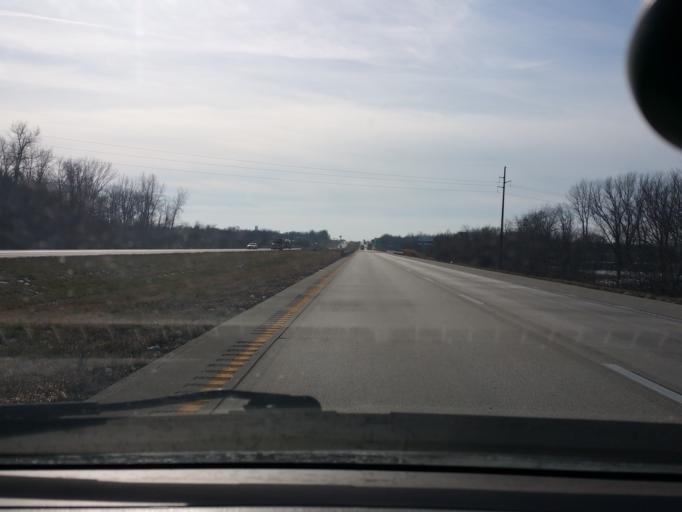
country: US
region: Missouri
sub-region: Clay County
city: Kearney
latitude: 39.3909
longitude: -94.3600
